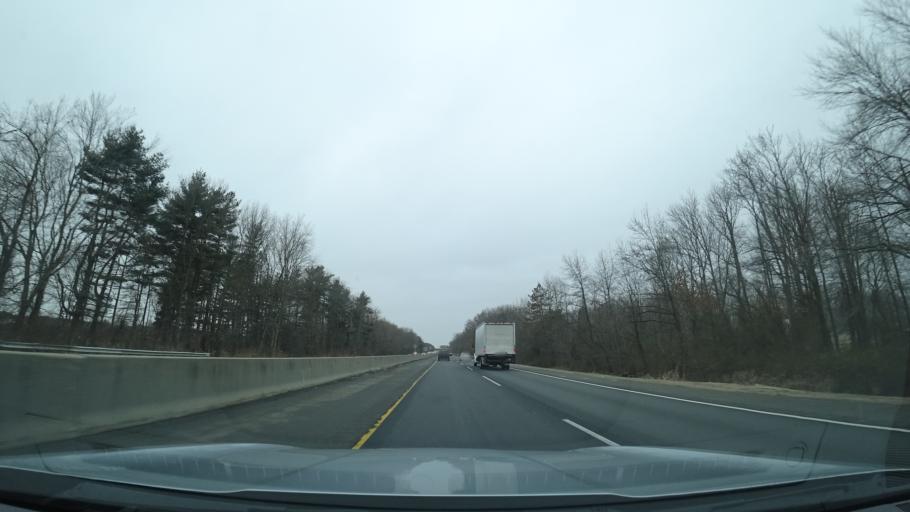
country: US
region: New Jersey
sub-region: Salem County
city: Carneys Point
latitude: 39.6891
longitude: -75.4268
